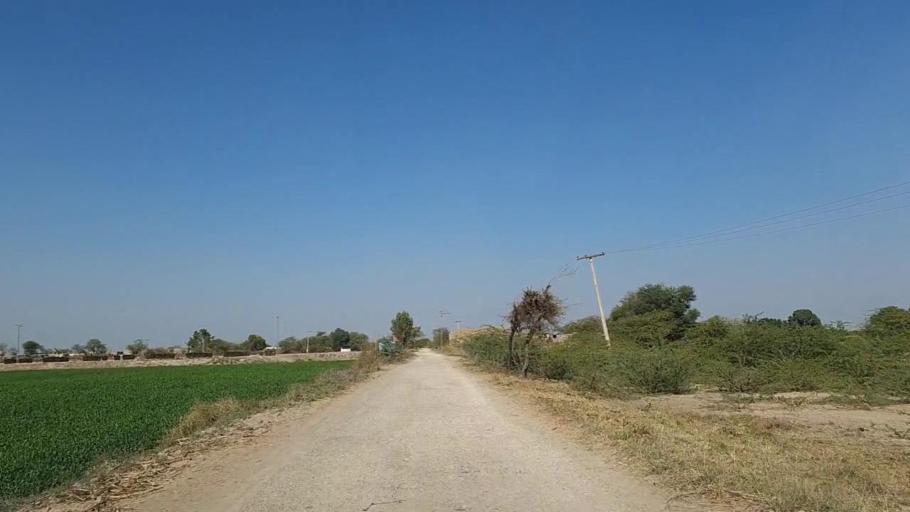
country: PK
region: Sindh
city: Nawabshah
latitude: 26.2524
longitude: 68.4411
